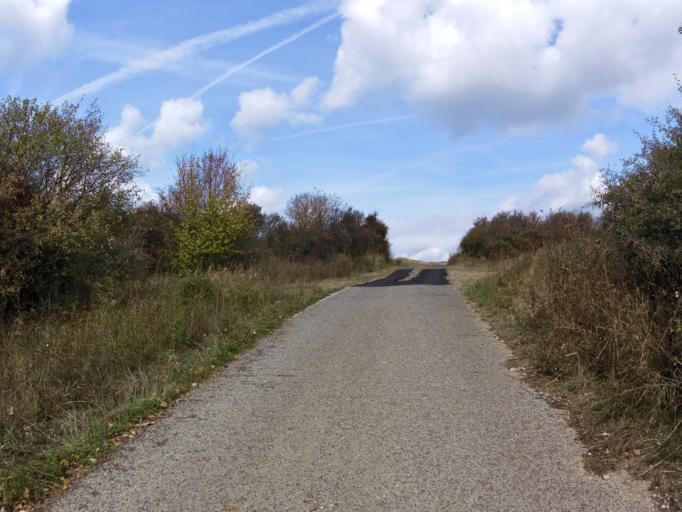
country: DE
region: Bavaria
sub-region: Regierungsbezirk Unterfranken
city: Reichenberg
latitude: 49.7319
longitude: 9.9436
